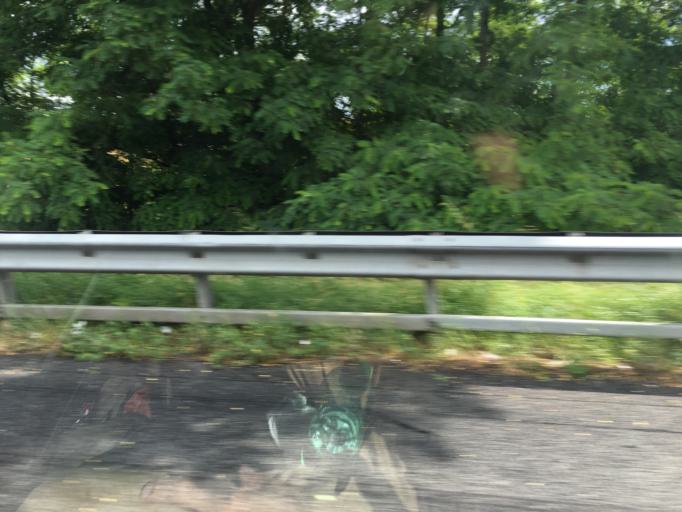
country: IT
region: Latium
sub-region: Citta metropolitana di Roma Capitale
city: Valmontone
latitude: 41.7605
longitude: 12.9500
